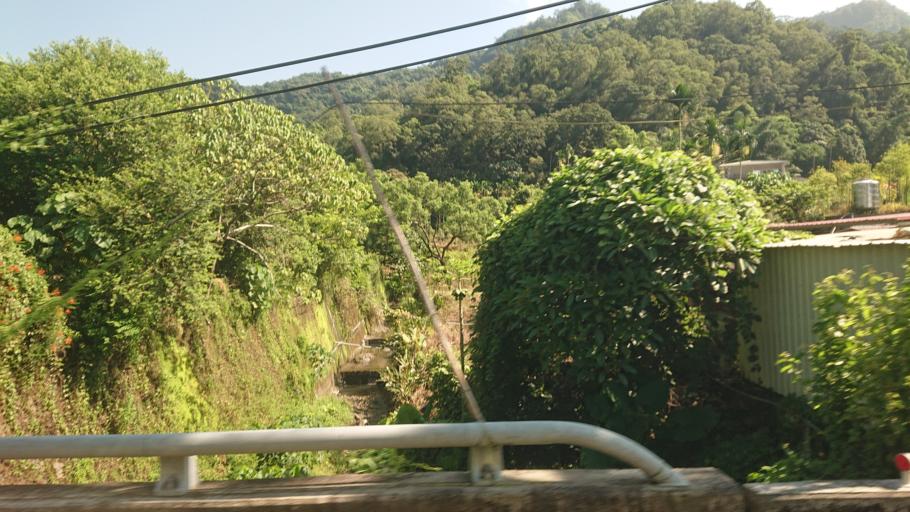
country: TW
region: Taiwan
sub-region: Nantou
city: Puli
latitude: 24.0618
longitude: 120.8891
